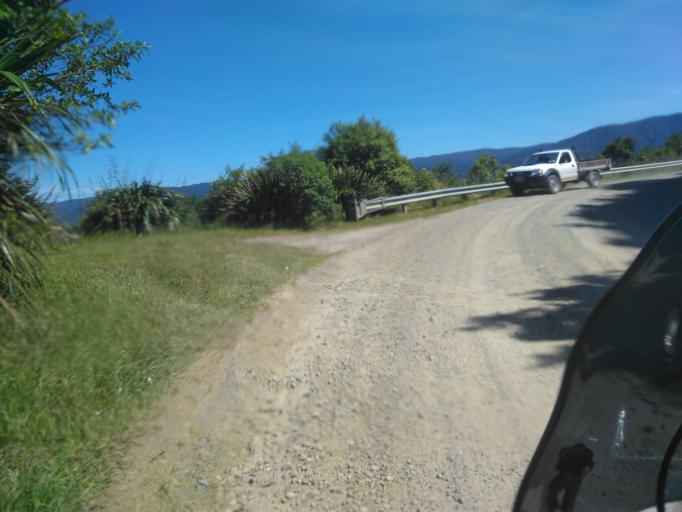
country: NZ
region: Hawke's Bay
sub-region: Wairoa District
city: Wairoa
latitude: -38.7937
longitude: 177.1244
